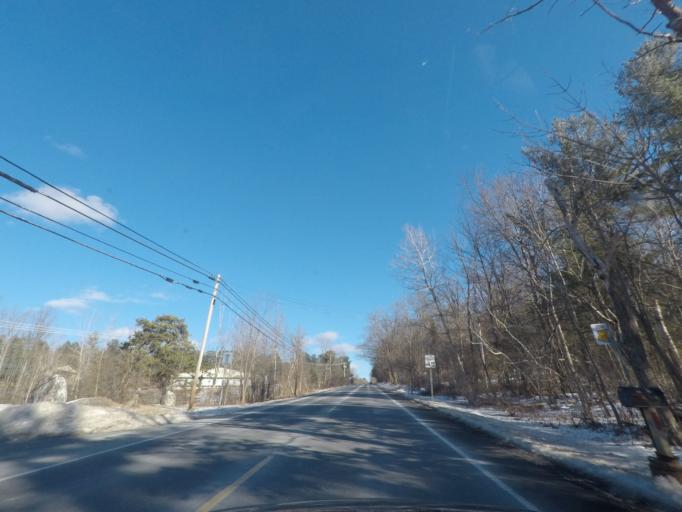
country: US
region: New York
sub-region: Columbia County
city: Chatham
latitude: 42.3205
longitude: -73.5370
